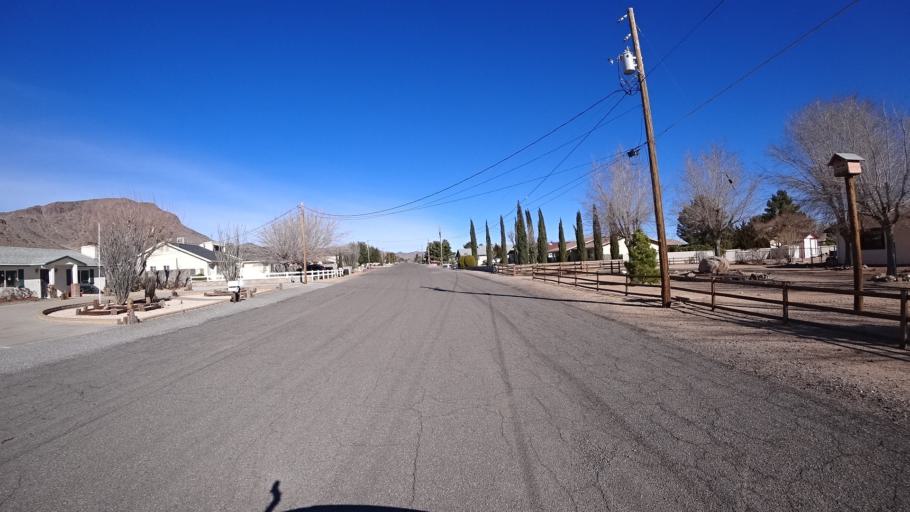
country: US
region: Arizona
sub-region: Mohave County
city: New Kingman-Butler
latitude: 35.2617
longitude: -114.0412
